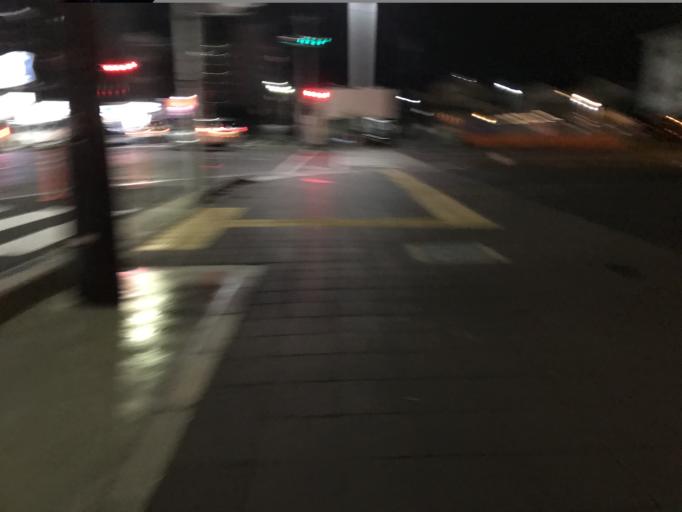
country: JP
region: Shiga Prefecture
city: Otsu-shi
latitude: 35.0130
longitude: 135.8625
